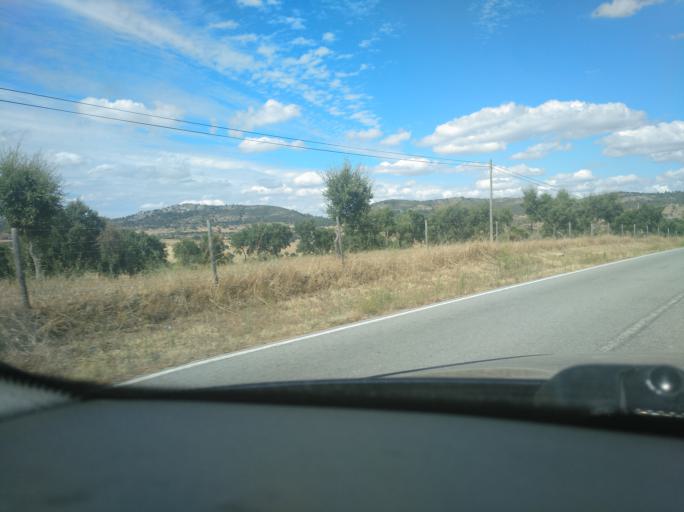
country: PT
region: Portalegre
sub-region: Arronches
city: Arronches
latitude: 39.1453
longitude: -7.2234
